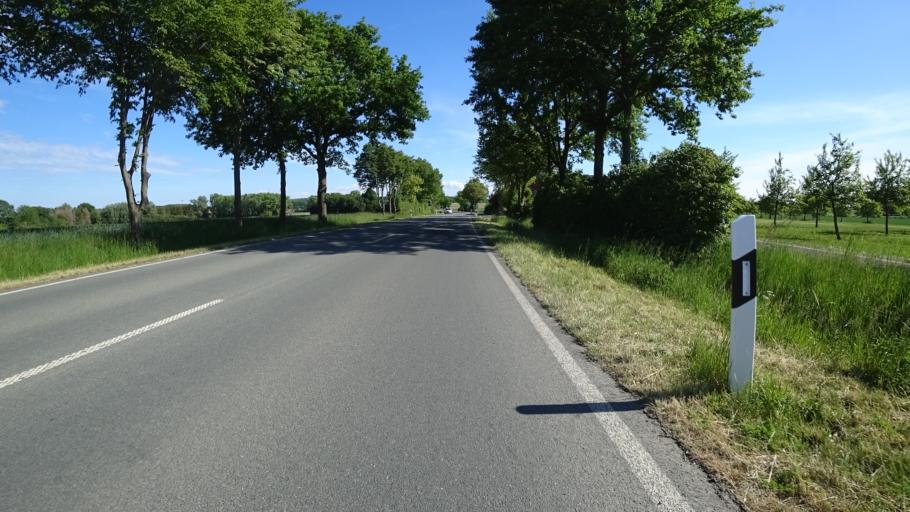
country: DE
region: North Rhine-Westphalia
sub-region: Regierungsbezirk Munster
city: Wadersloh
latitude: 51.7970
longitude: 8.2149
